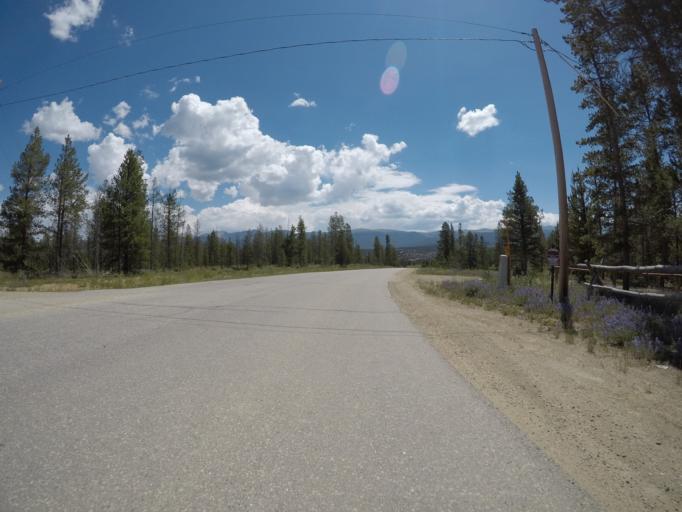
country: US
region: Colorado
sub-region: Grand County
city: Fraser
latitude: 39.9510
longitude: -105.8315
